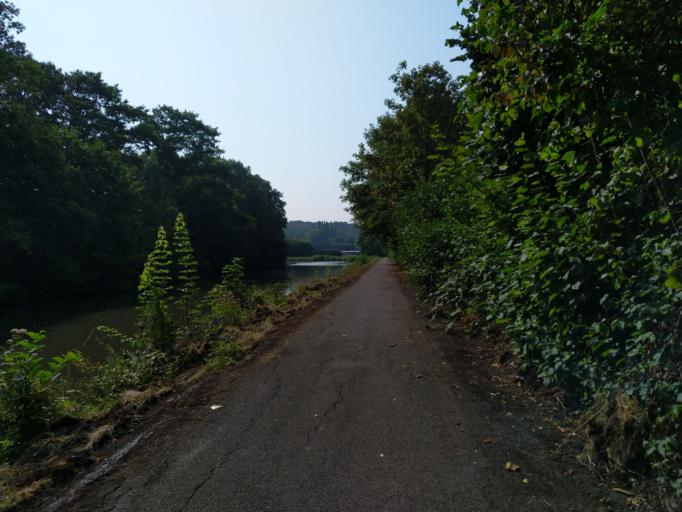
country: BE
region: Wallonia
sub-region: Province du Hainaut
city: Seneffe
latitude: 50.5172
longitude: 4.2667
